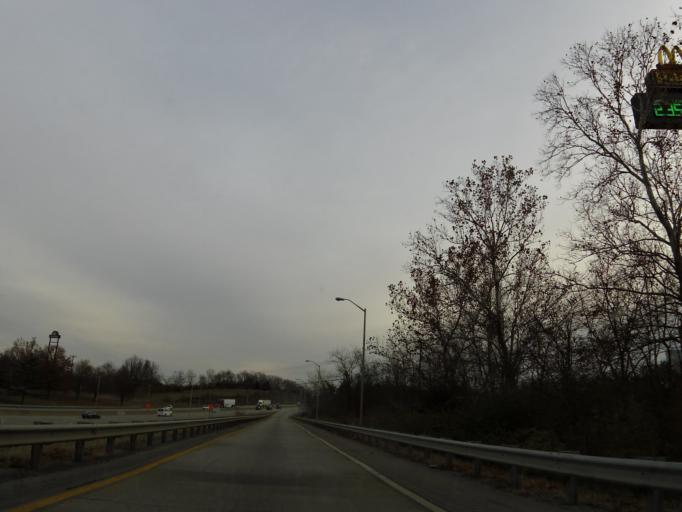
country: US
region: Kentucky
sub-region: Scott County
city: Georgetown
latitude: 38.2758
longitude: -84.5584
